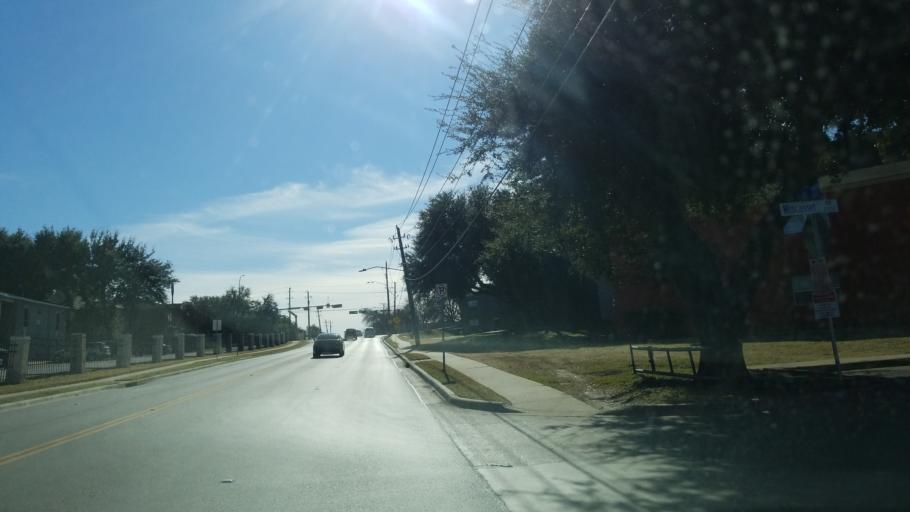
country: US
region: Texas
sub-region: Tarrant County
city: Arlington
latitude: 32.7220
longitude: -97.0572
